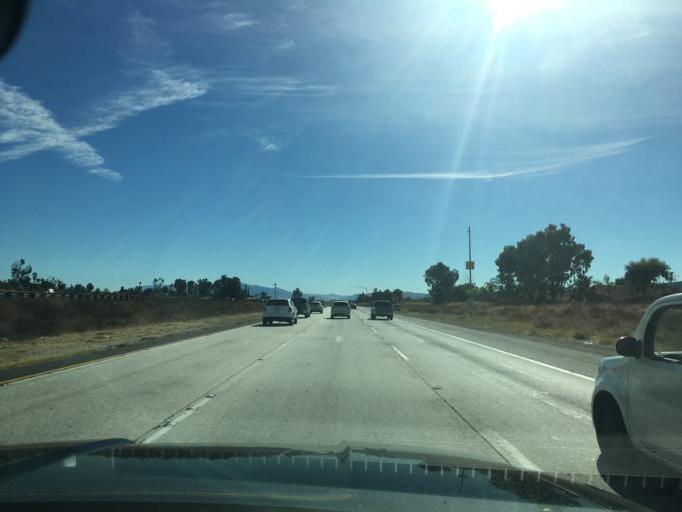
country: US
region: California
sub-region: Riverside County
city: Wildomar
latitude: 33.6114
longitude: -117.2595
